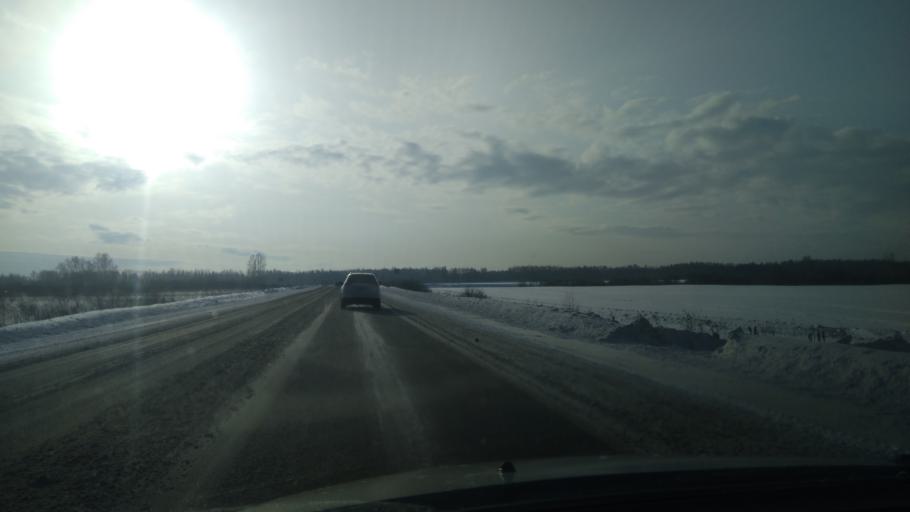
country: RU
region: Sverdlovsk
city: Bogdanovich
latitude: 56.7838
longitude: 61.9979
